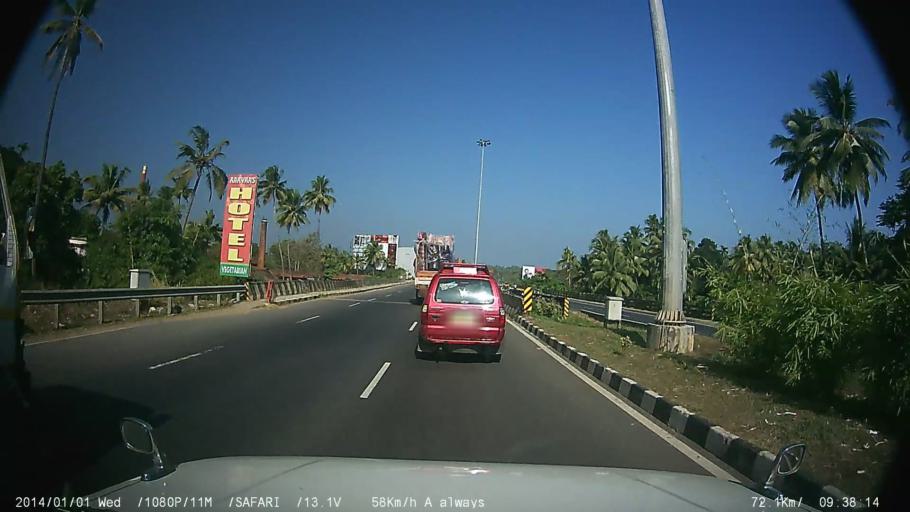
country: IN
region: Kerala
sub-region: Thrissur District
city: Irinjalakuda
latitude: 10.4111
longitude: 76.2727
